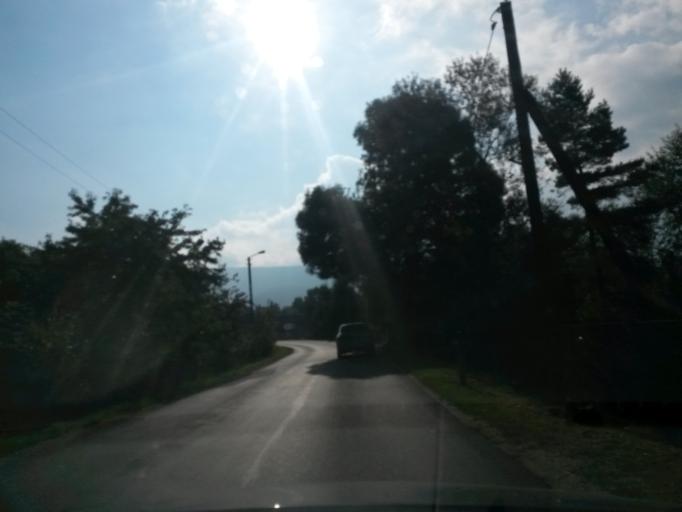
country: PL
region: Lower Silesian Voivodeship
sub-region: Powiat jeleniogorski
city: Karpacz
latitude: 50.7995
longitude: 15.7755
